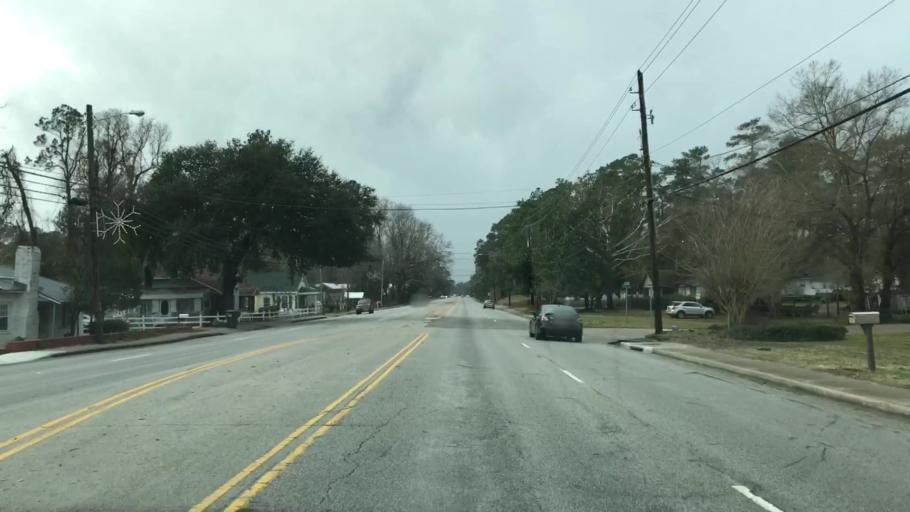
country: US
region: South Carolina
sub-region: Horry County
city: Conway
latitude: 33.8298
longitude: -79.0610
